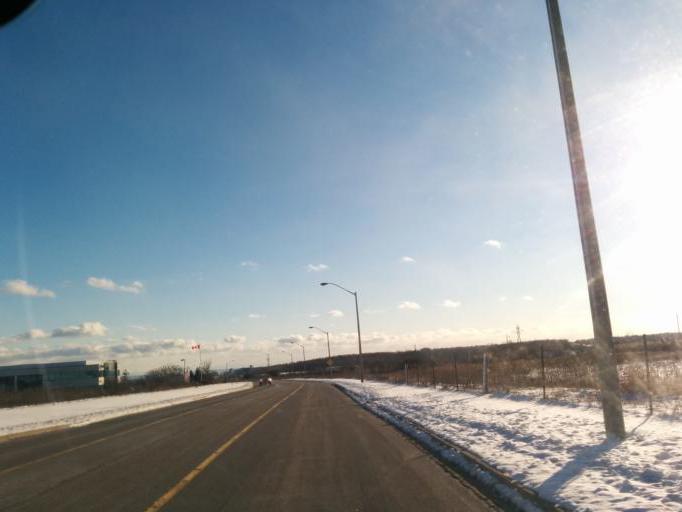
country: CA
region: Ontario
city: Oakville
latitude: 43.5015
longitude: -79.6710
